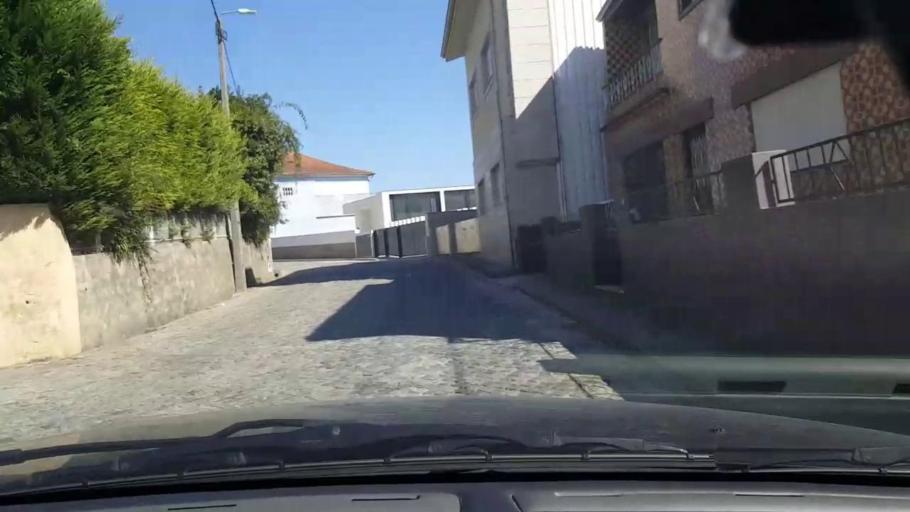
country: PT
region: Porto
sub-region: Matosinhos
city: Lavra
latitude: 41.2947
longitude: -8.6927
